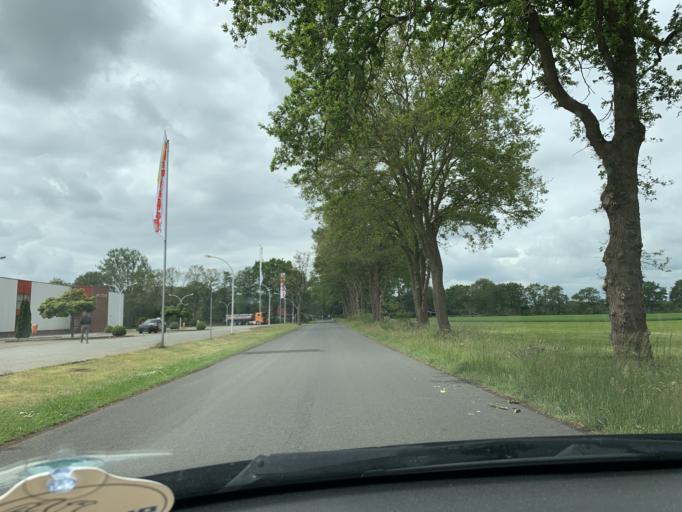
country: DE
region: Lower Saxony
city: Bockhorn
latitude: 53.3590
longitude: 8.0683
